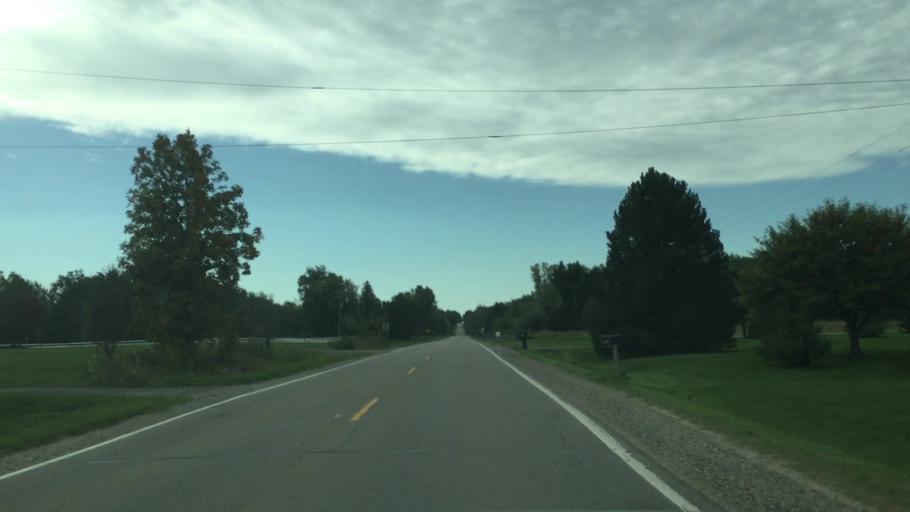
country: US
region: Michigan
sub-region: Livingston County
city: Howell
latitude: 42.6708
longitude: -83.8771
